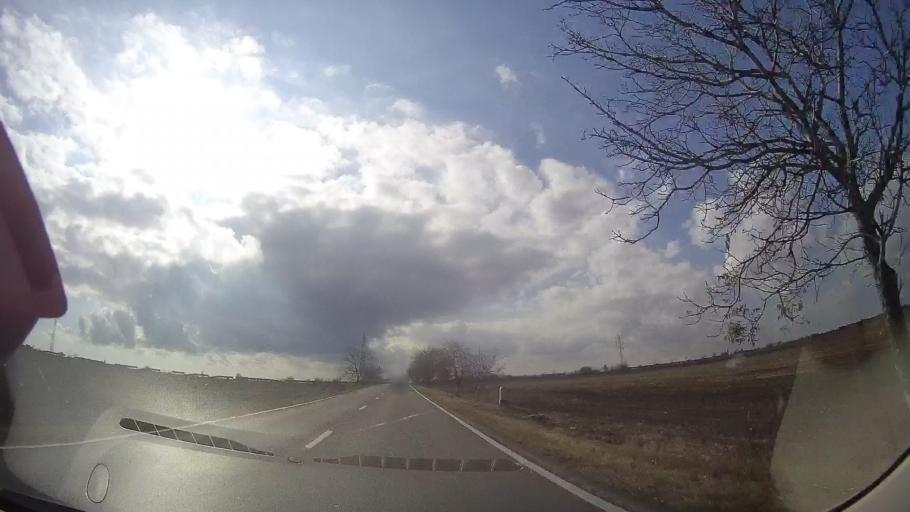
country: RO
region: Constanta
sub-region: Comuna Agigea
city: Agigea
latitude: 44.0749
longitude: 28.5993
